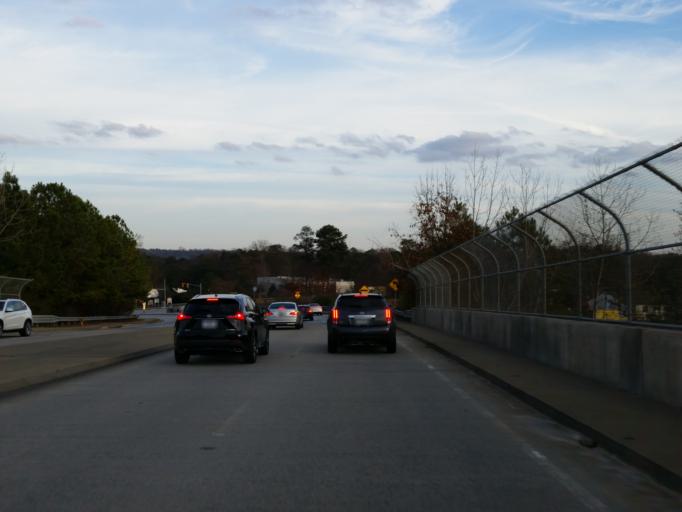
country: US
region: Georgia
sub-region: Cobb County
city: Vinings
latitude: 33.8488
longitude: -84.4857
